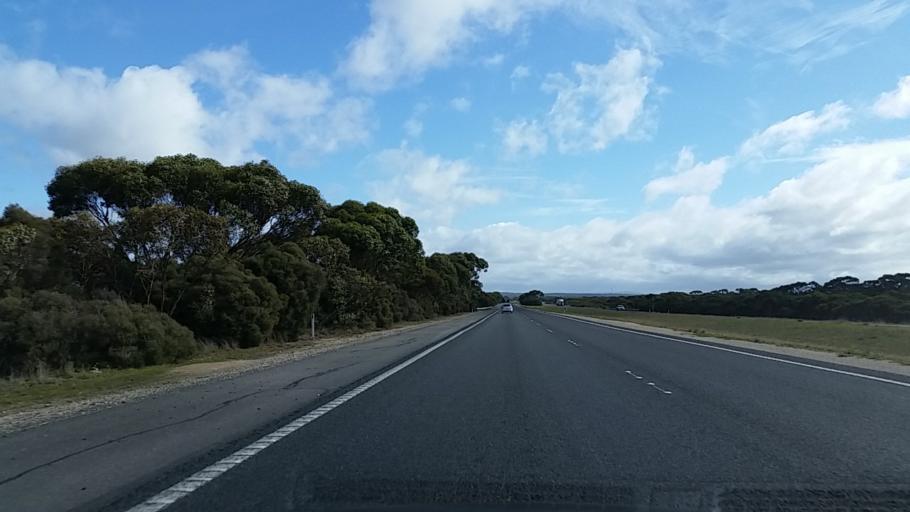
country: AU
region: South Australia
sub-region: Murray Bridge
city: Murray Bridge
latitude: -35.1447
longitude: 139.1574
